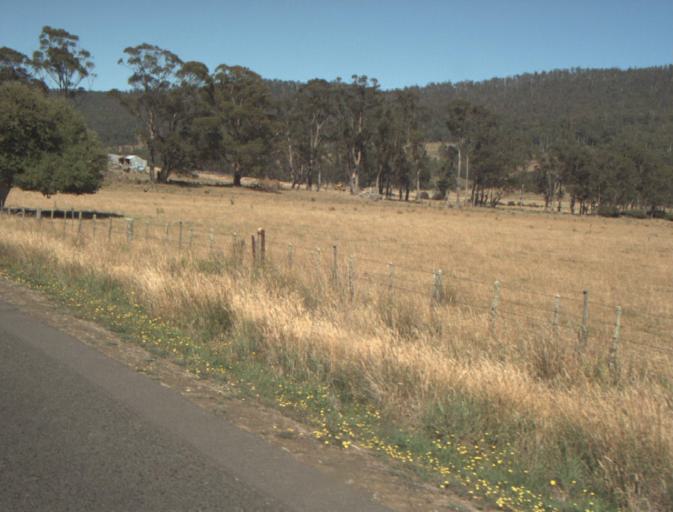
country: AU
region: Tasmania
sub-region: Launceston
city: Newstead
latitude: -41.3332
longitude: 147.3067
